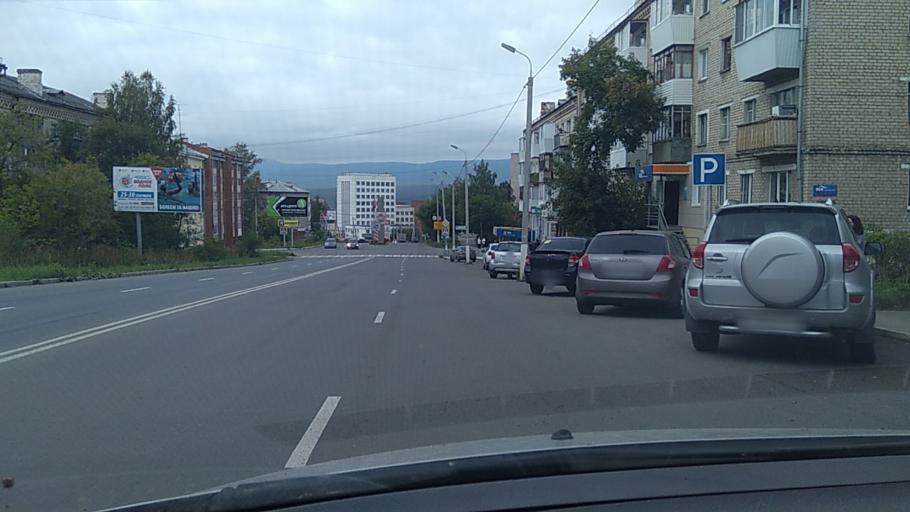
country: RU
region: Chelyabinsk
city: Zlatoust
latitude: 55.1142
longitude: 59.7168
